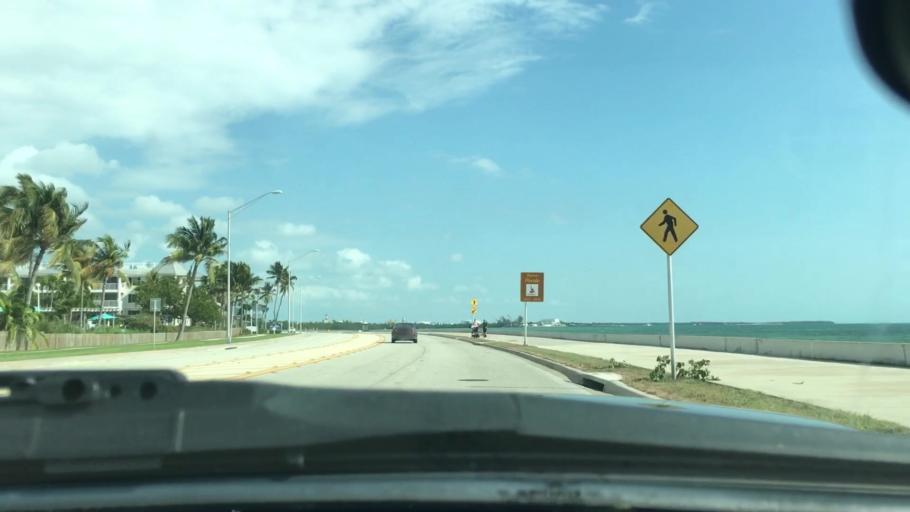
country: US
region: Florida
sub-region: Monroe County
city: Stock Island
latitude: 24.5528
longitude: -81.7516
